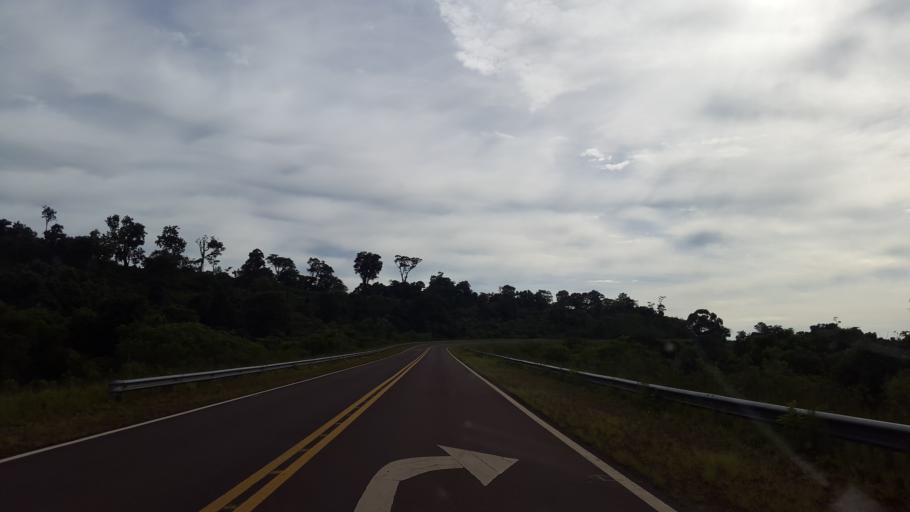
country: AR
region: Misiones
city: Bernardo de Irigoyen
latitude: -26.3850
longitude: -53.7975
